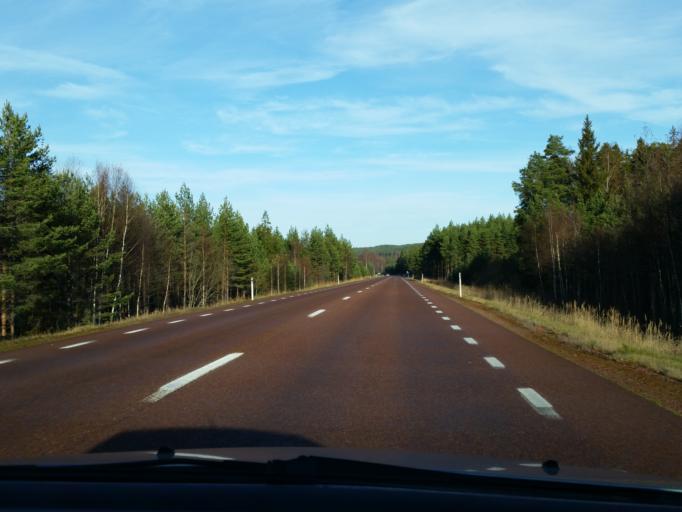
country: AX
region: Alands landsbygd
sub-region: Finstroem
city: Finstroem
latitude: 60.2884
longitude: 19.9530
